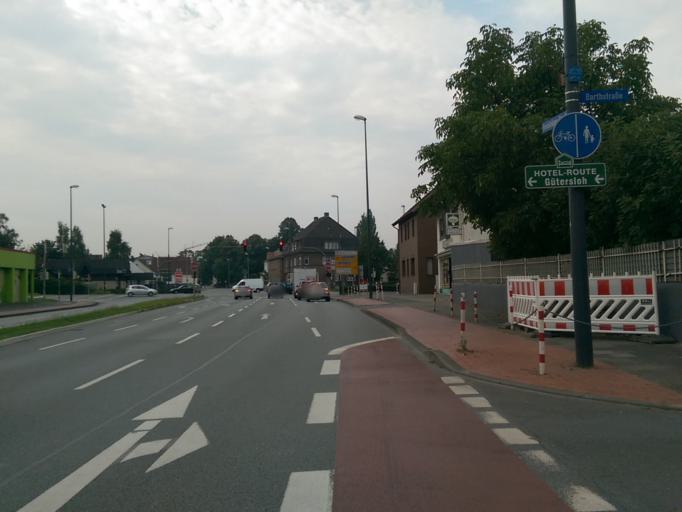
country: DE
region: North Rhine-Westphalia
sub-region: Regierungsbezirk Detmold
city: Guetersloh
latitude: 51.9149
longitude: 8.3717
